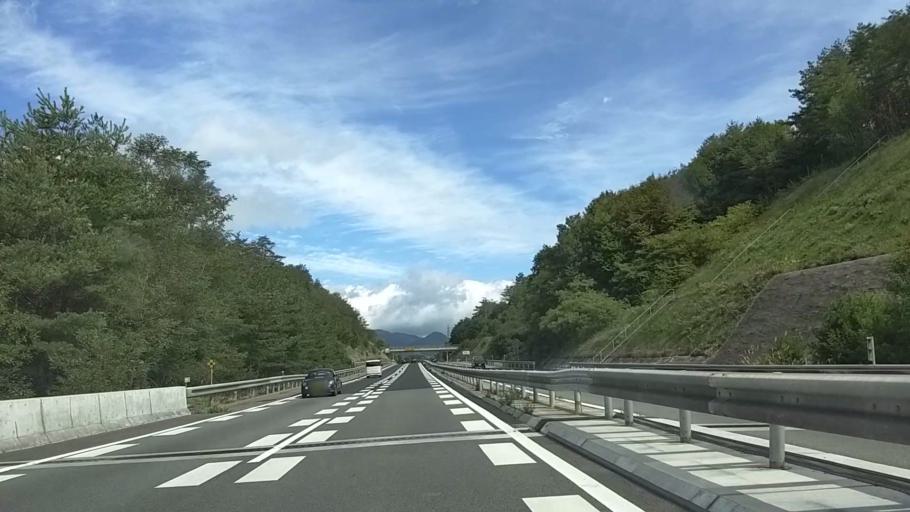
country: JP
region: Nagano
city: Hotaka
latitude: 36.4149
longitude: 138.0030
